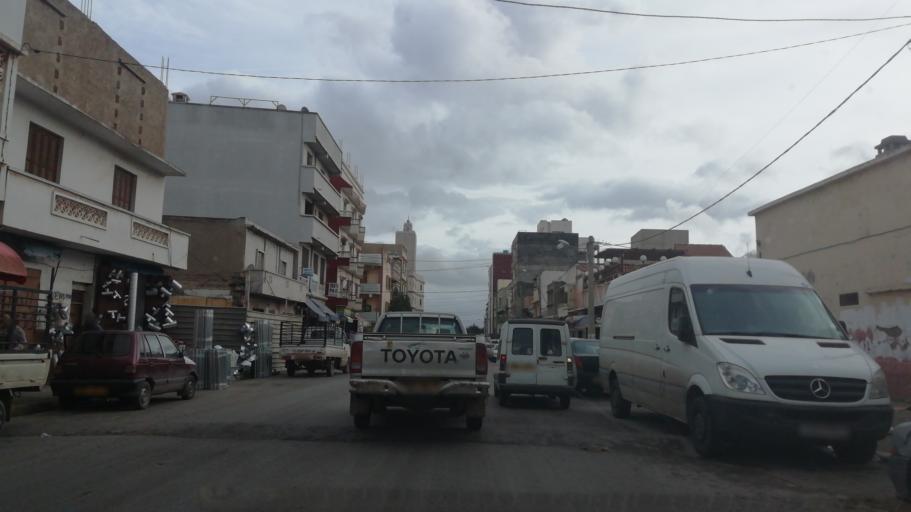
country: DZ
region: Oran
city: Oran
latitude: 35.6853
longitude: -0.6430
